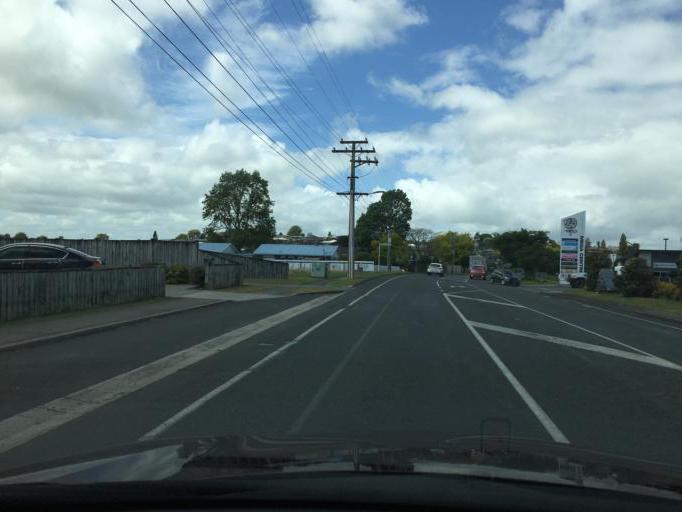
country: NZ
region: Waikato
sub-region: Waipa District
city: Cambridge
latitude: -38.0065
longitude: 175.3392
